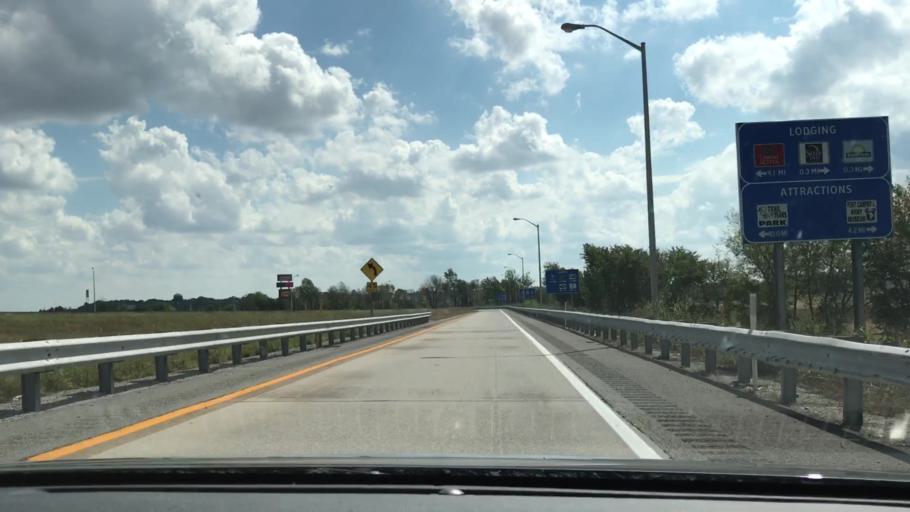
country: US
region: Kentucky
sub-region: Christian County
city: Oak Grove
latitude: 36.7034
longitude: -87.4587
